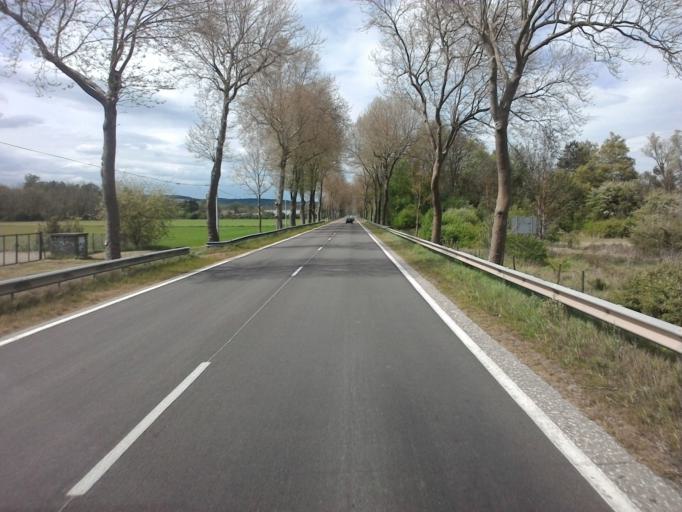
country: FR
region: Bourgogne
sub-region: Departement de l'Yonne
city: Champs-sur-Yonne
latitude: 47.7154
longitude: 3.6180
